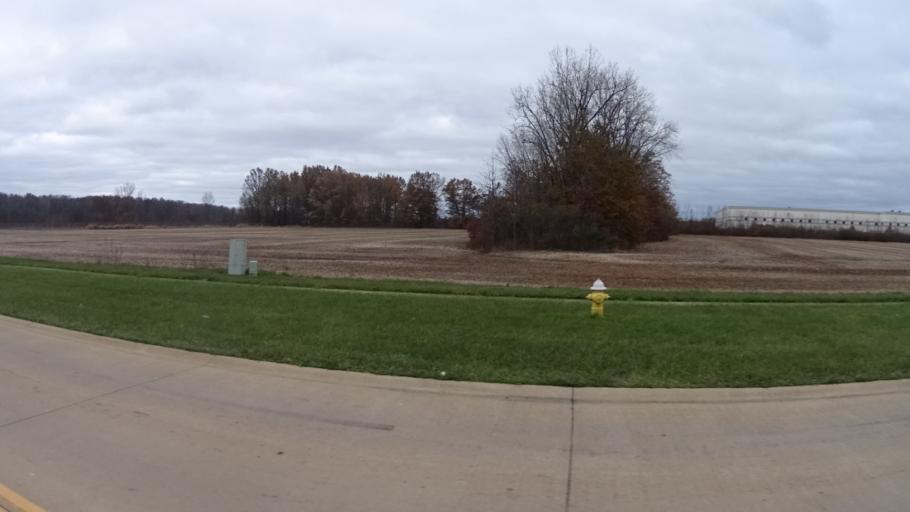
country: US
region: Ohio
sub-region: Lorain County
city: Avon Lake
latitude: 41.4819
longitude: -82.0311
